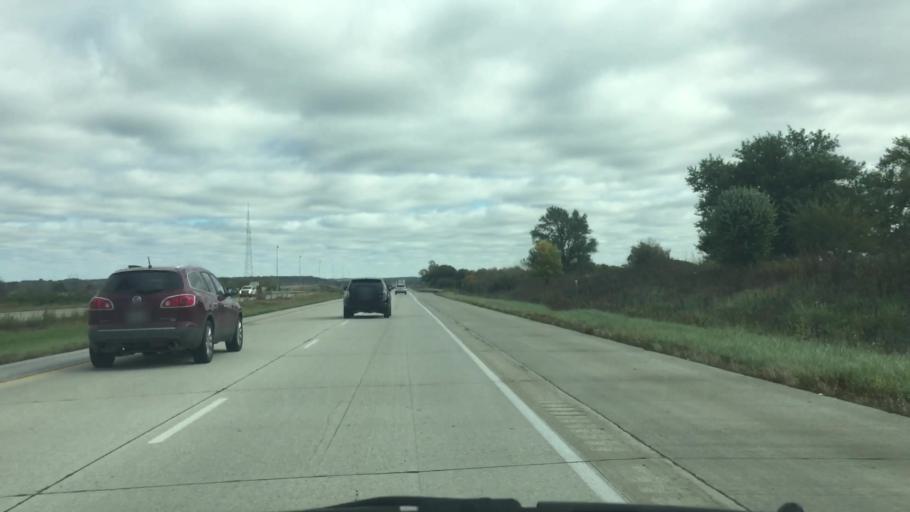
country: US
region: Iowa
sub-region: Polk County
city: Mitchellville
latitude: 41.6806
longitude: -93.3511
